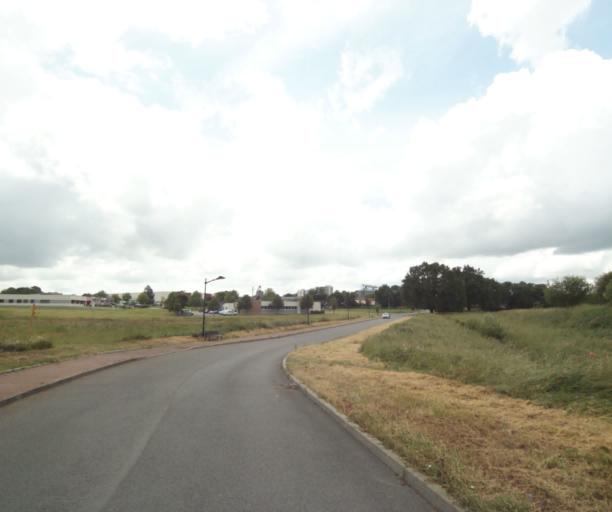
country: FR
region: Pays de la Loire
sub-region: Departement de la Sarthe
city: Solesmes
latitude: 47.8409
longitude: -0.3136
